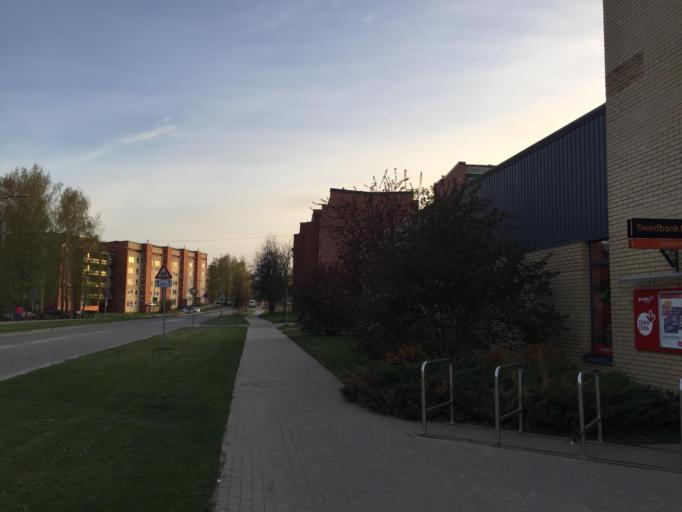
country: LV
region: Valmieras Rajons
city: Valmiera
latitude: 57.5469
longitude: 25.4197
